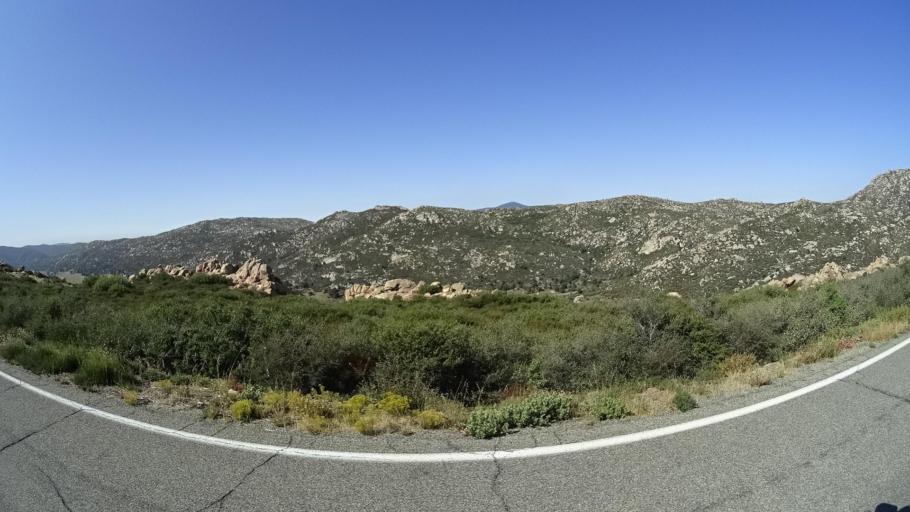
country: US
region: California
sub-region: San Diego County
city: Pine Valley
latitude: 32.9632
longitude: -116.5115
